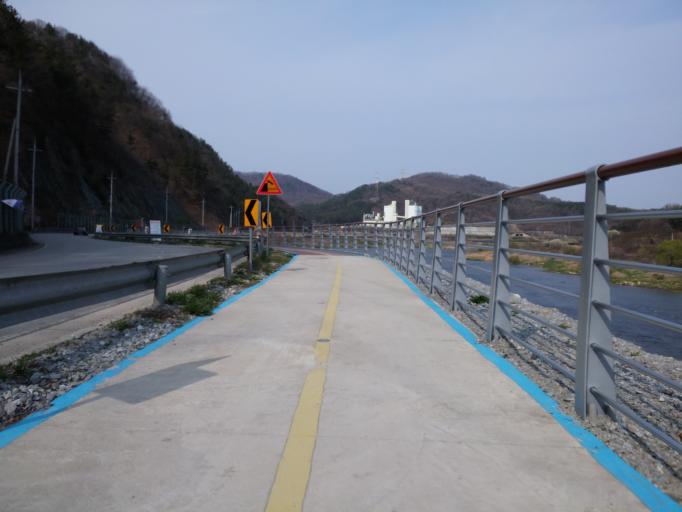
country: KR
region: Daejeon
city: Songgang-dong
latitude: 36.4968
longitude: 127.3766
